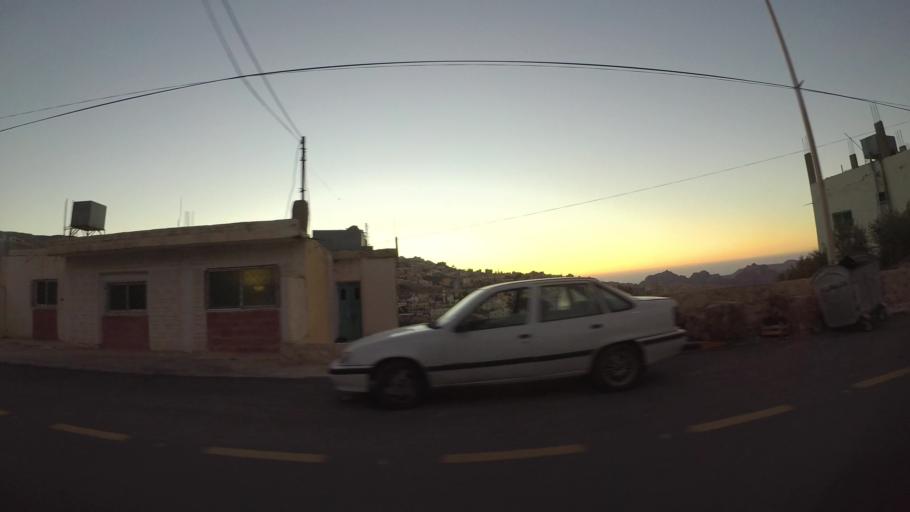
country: JO
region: Ma'an
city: Petra
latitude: 30.3161
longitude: 35.4824
